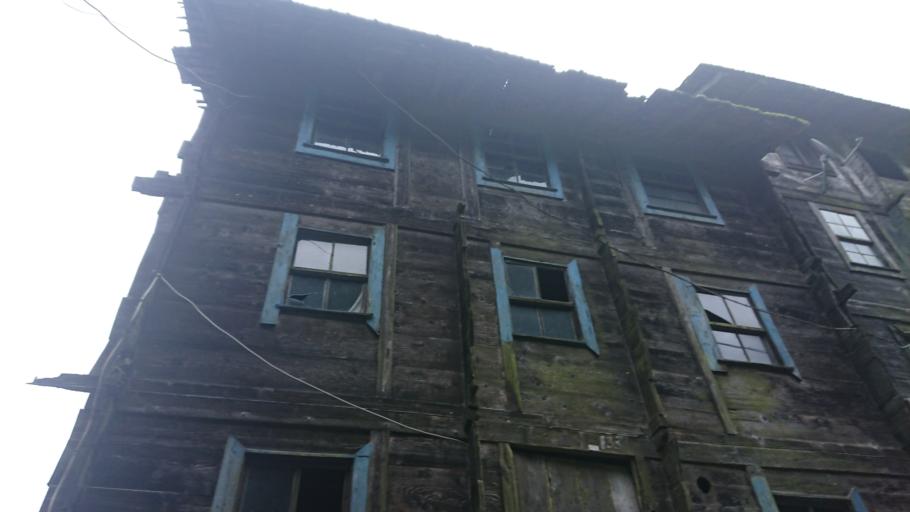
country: TR
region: Rize
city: Ikizdere
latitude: 40.8593
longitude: 40.5864
